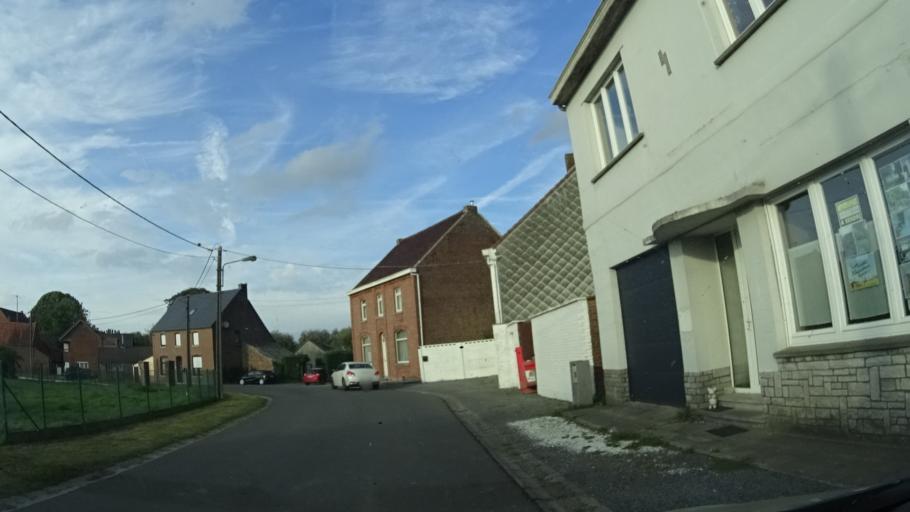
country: BE
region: Wallonia
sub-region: Province du Hainaut
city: Peruwelz
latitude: 50.5824
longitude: 3.5807
